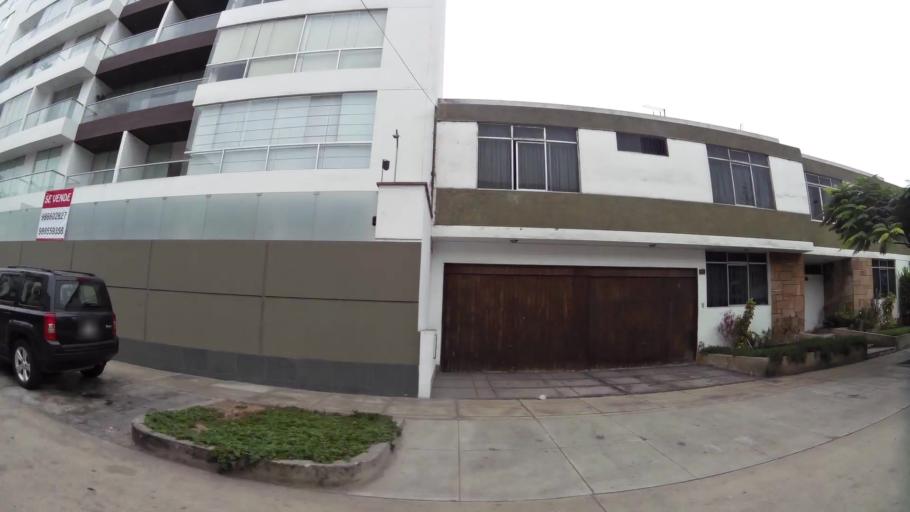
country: PE
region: Lima
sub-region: Lima
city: San Luis
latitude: -12.1017
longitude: -77.0147
